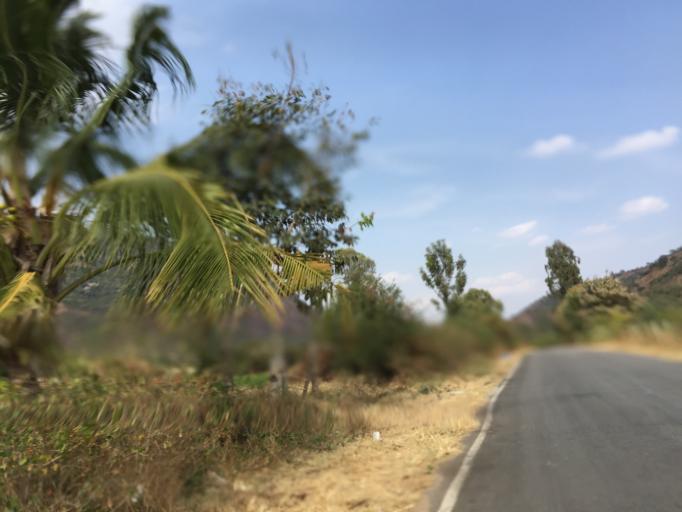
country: IN
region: Karnataka
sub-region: Chikkaballapur
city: Chik Ballapur
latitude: 13.3682
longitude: 77.6610
